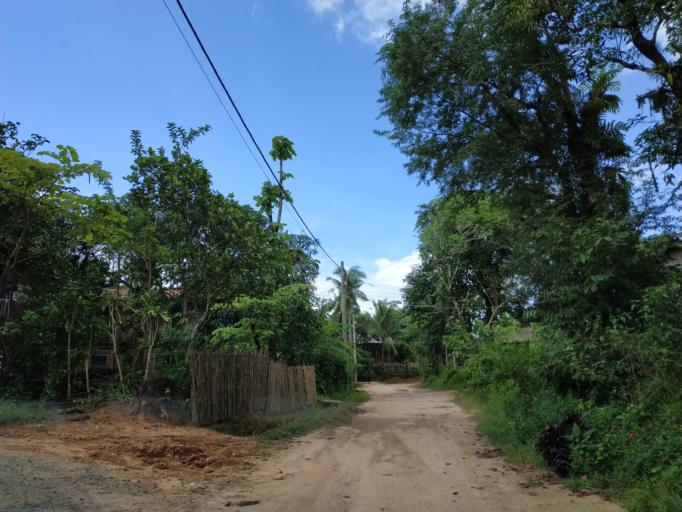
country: MM
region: Tanintharyi
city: Dawei
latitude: 14.1874
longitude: 98.1643
